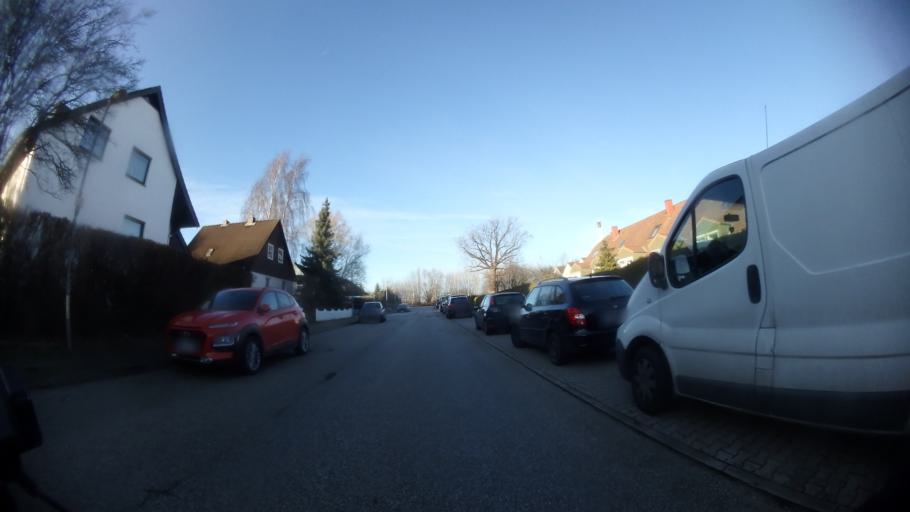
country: DE
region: Schleswig-Holstein
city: Travemuende
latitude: 53.9690
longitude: 10.8620
